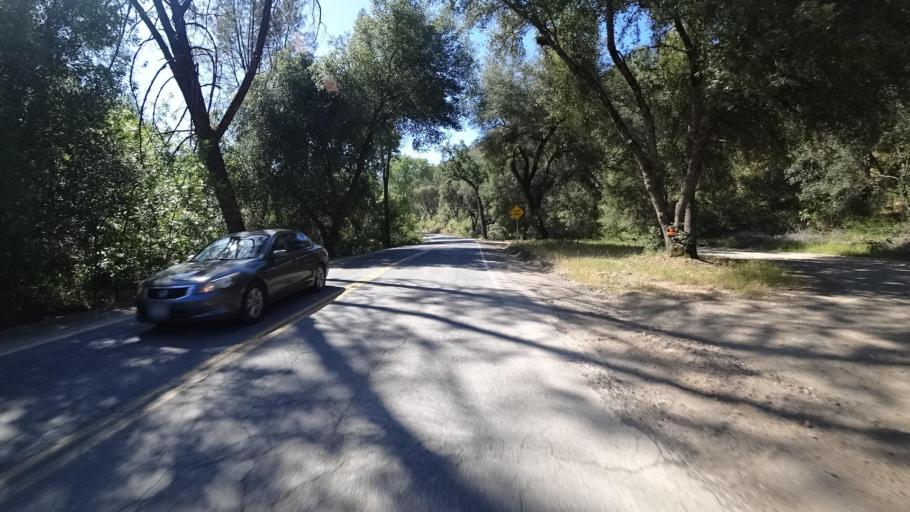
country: US
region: California
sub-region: Lake County
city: Clearlake Oaks
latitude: 39.0433
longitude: -122.5762
